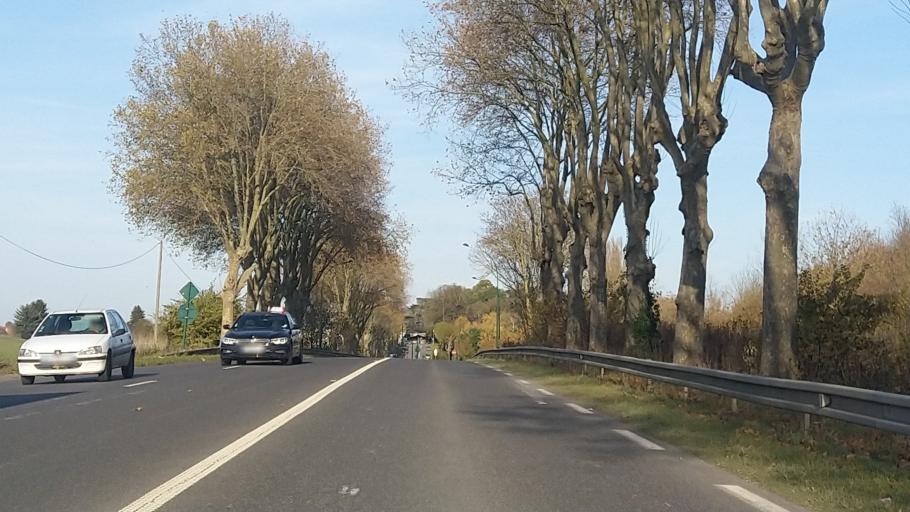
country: FR
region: Ile-de-France
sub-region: Departement du Val-d'Oise
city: Ecouen
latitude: 49.0415
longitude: 2.3963
